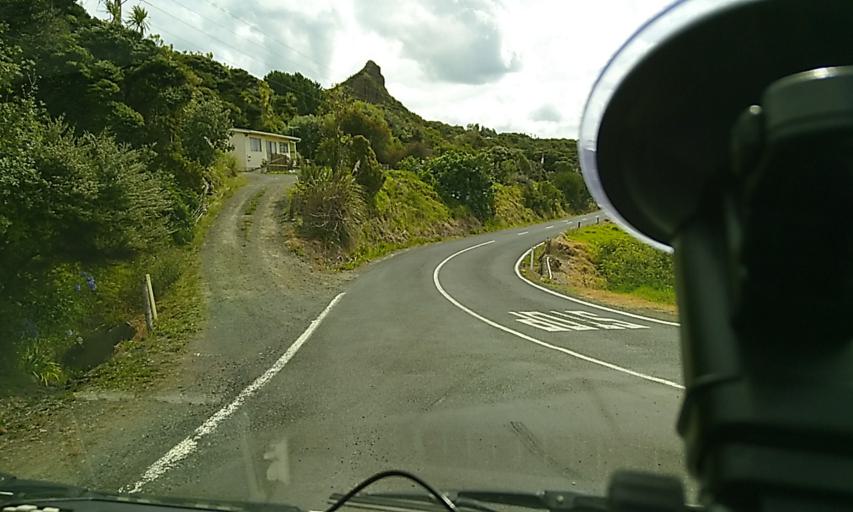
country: NZ
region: Northland
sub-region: Far North District
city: Ahipara
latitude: -35.5379
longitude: 173.3833
